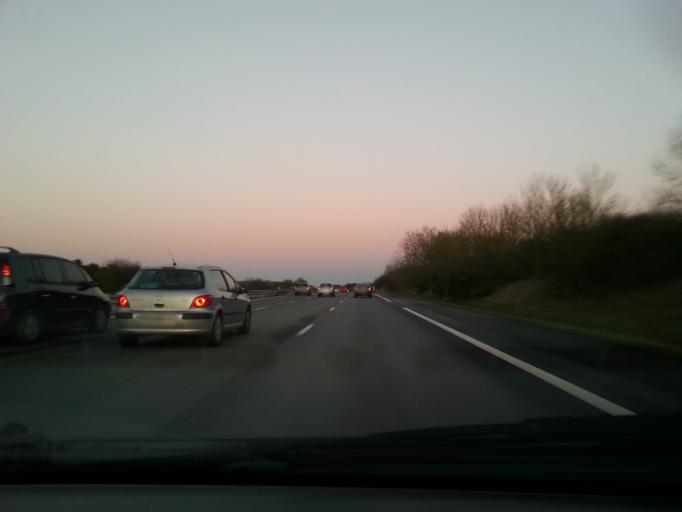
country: FR
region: Centre
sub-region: Departement d'Eure-et-Loir
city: Gallardon
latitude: 48.4871
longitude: 1.6613
